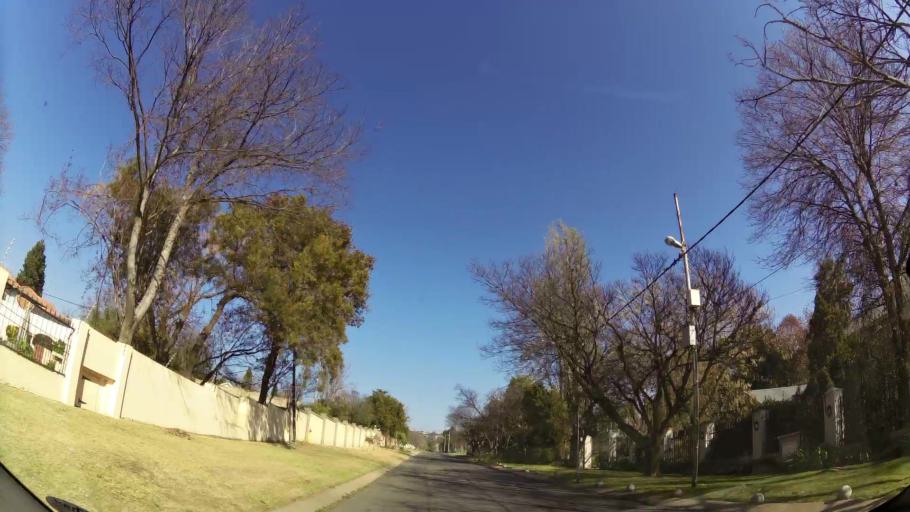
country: ZA
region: Gauteng
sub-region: City of Johannesburg Metropolitan Municipality
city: Midrand
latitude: -26.0463
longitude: 28.0455
